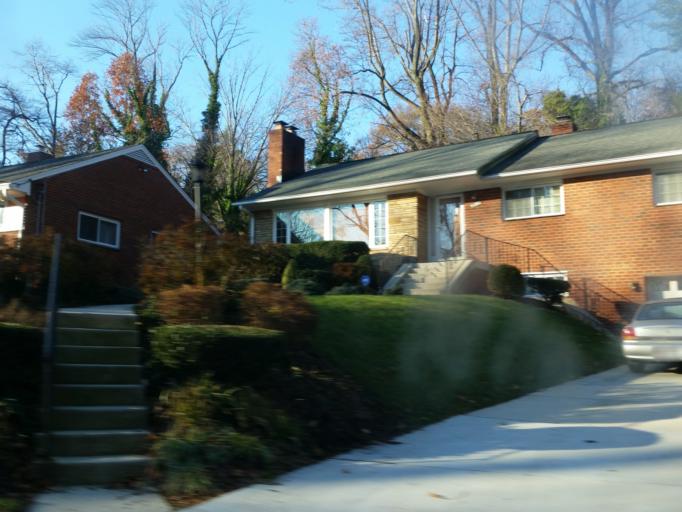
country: US
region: Maryland
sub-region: Montgomery County
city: Silver Spring
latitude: 38.9894
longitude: -77.0443
